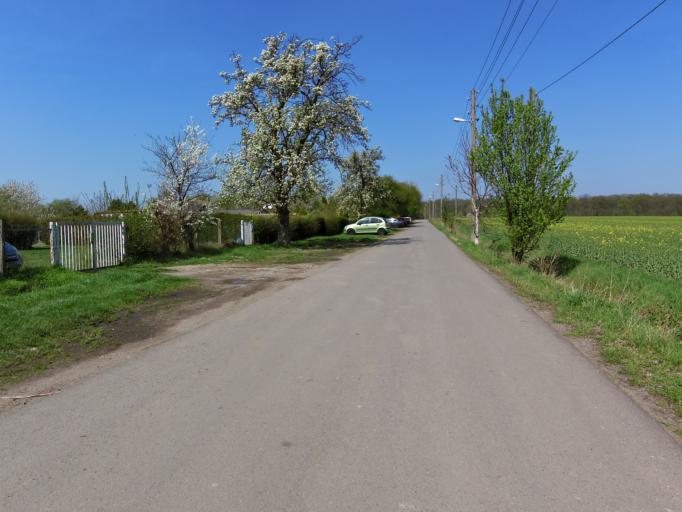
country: DE
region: Saxony
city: Leipzig
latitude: 51.3934
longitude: 12.3175
